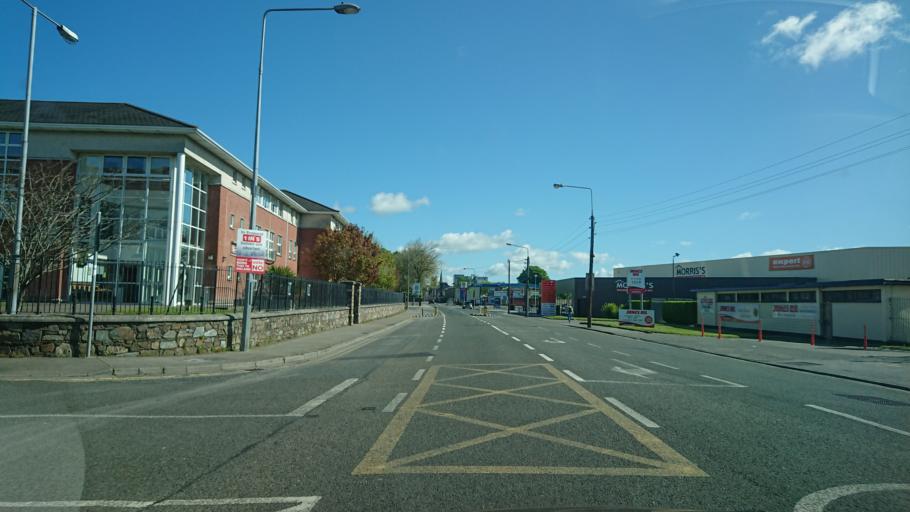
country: IE
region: Munster
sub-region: Waterford
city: Waterford
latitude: 52.2518
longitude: -7.1169
